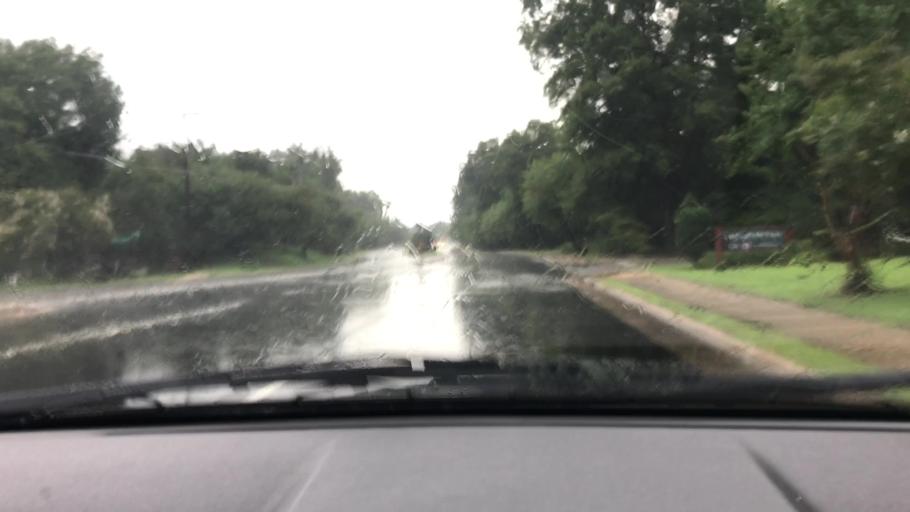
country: US
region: Virginia
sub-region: Henrico County
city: Short Pump
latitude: 37.6579
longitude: -77.5622
